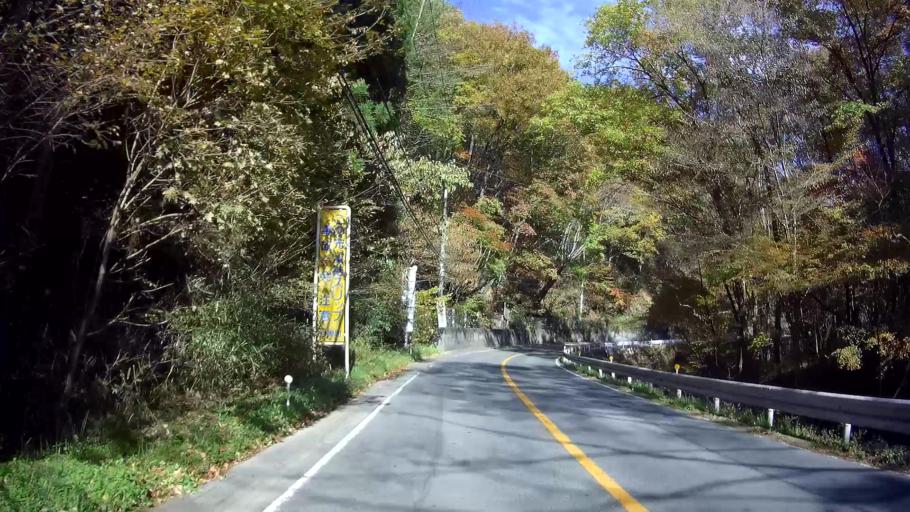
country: JP
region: Gunma
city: Nakanojomachi
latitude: 36.4898
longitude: 138.7738
